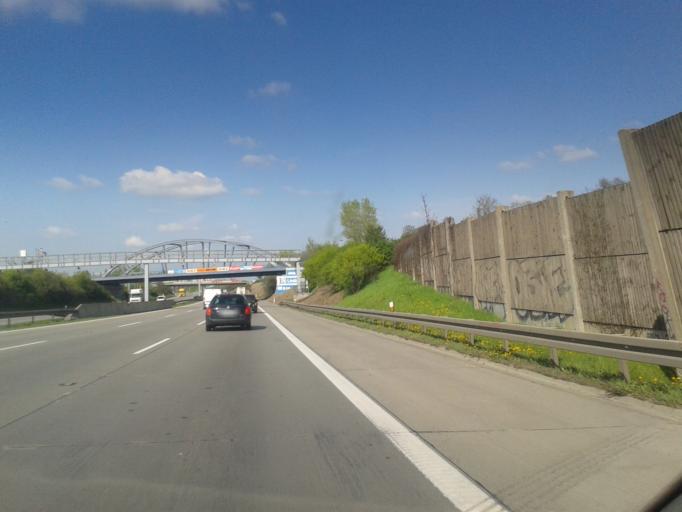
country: CZ
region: Central Bohemia
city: Hostivice
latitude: 50.0677
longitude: 14.2820
